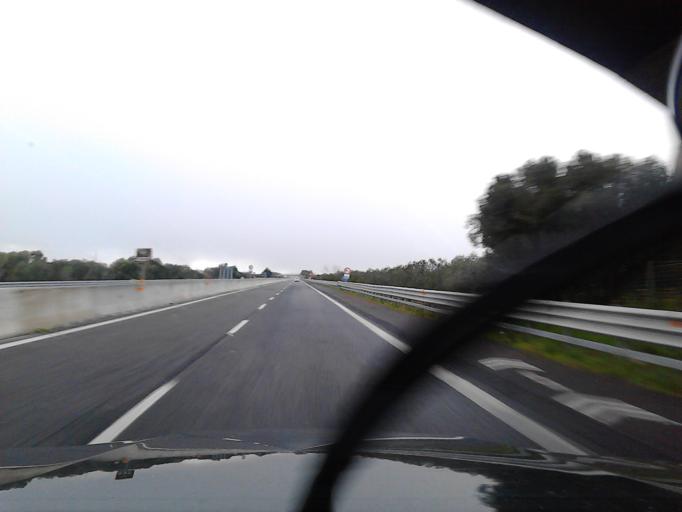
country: IT
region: Apulia
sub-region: Provincia di Bari
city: Bitonto
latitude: 41.1423
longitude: 16.6858
